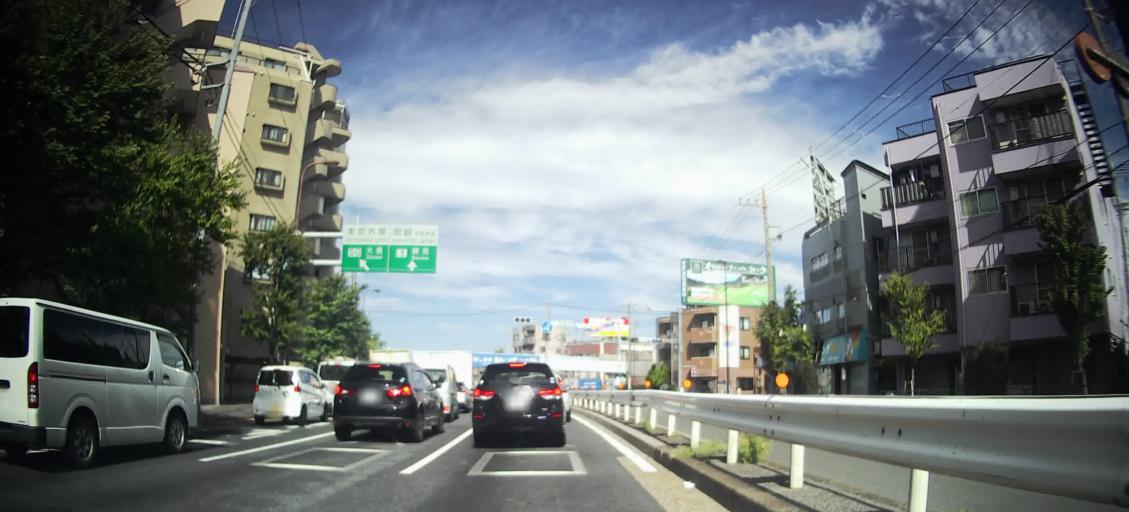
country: JP
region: Saitama
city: Wako
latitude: 35.7539
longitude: 139.6083
